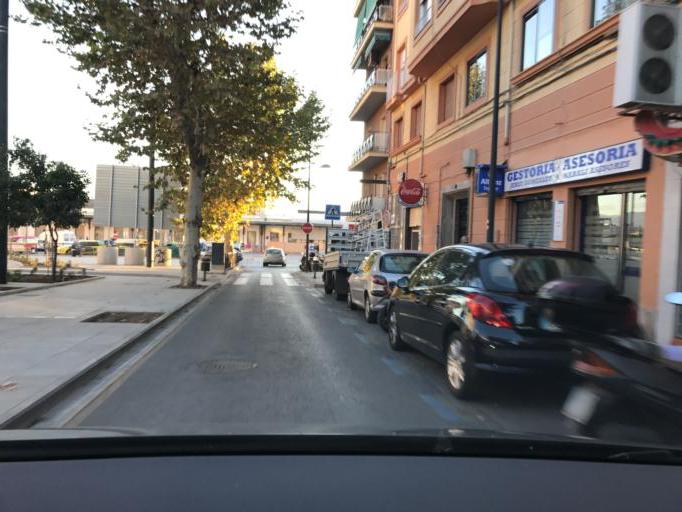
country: ES
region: Andalusia
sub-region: Provincia de Granada
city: Granada
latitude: 37.1851
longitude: -3.6088
